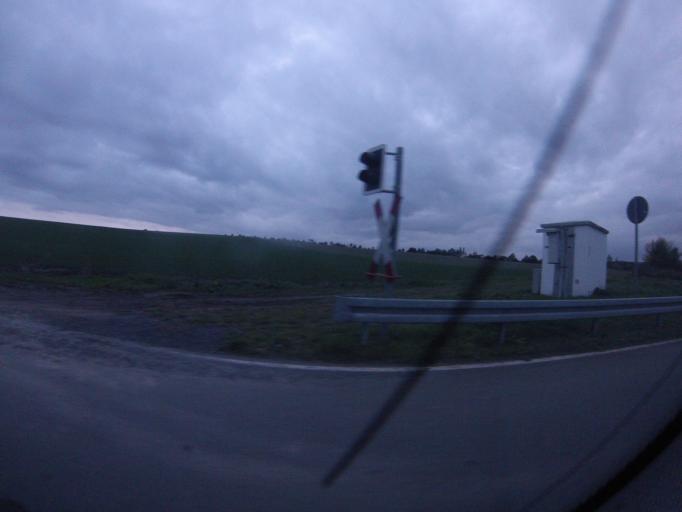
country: DE
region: Thuringia
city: Saara
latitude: 50.9268
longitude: 12.4271
